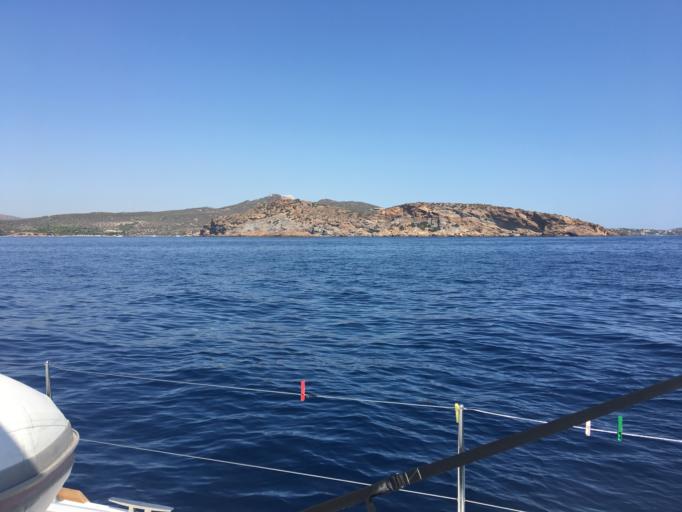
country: GR
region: Attica
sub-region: Nomarchia Anatolikis Attikis
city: Lavrio
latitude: 37.6400
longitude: 24.0262
